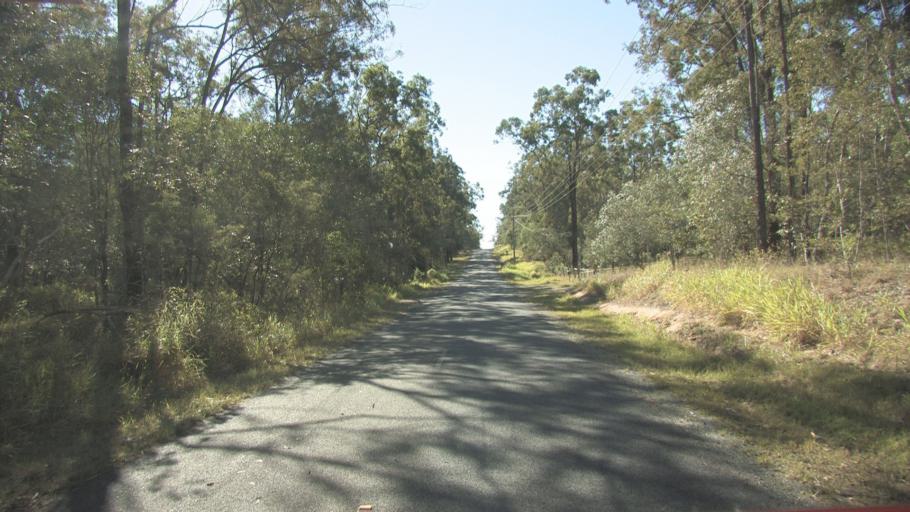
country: AU
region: Queensland
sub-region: Logan
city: Chambers Flat
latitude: -27.8147
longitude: 153.0711
